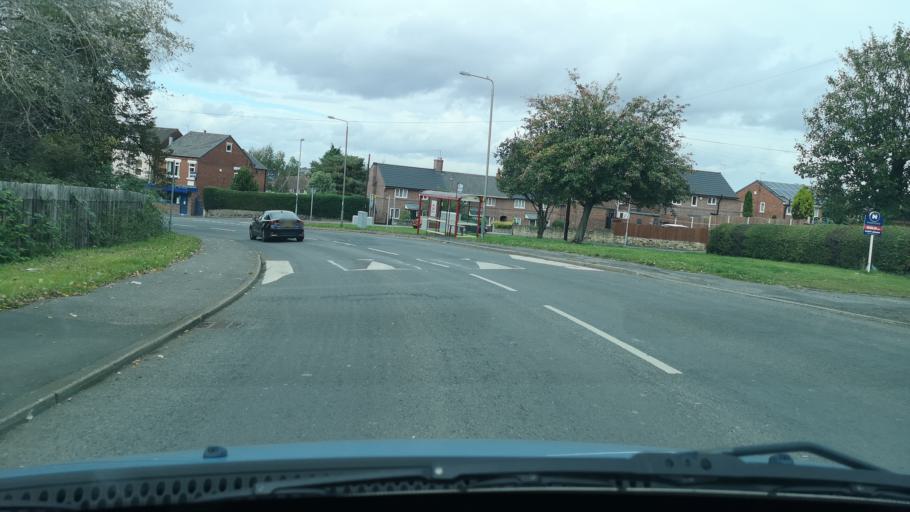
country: GB
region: England
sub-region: City and Borough of Wakefield
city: Featherstone
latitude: 53.6707
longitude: -1.3491
